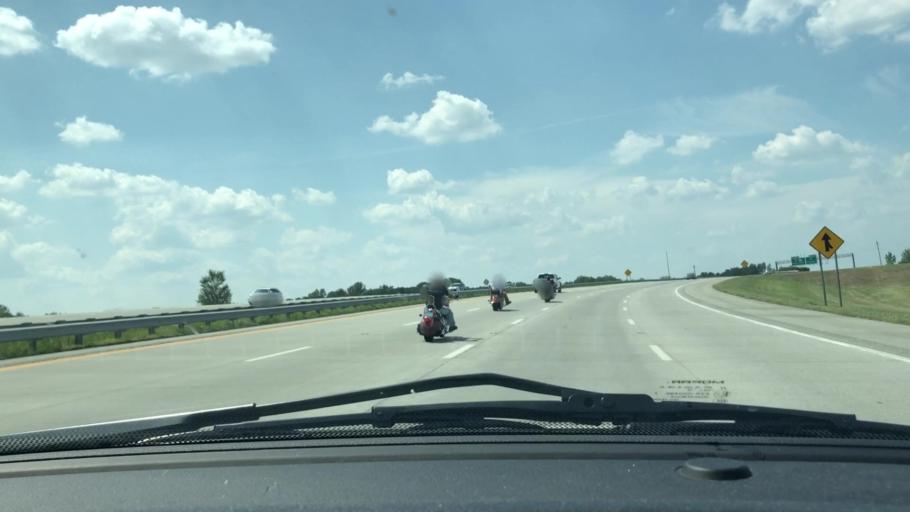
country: US
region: North Carolina
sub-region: Guilford County
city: Jamestown
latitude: 36.0475
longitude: -79.9131
